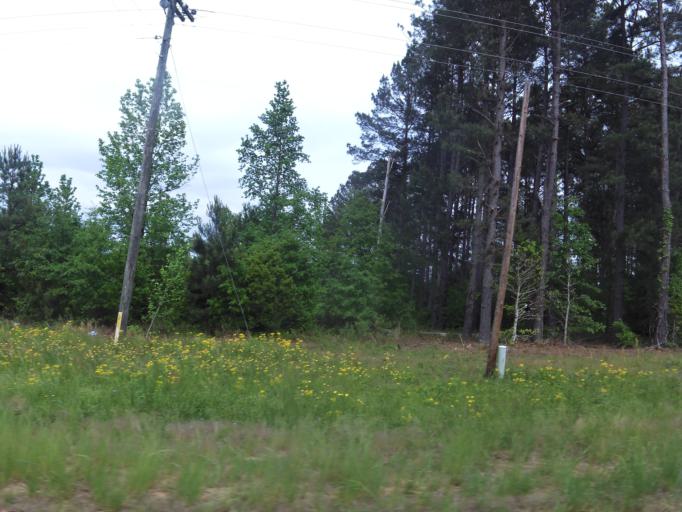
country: US
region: Georgia
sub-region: McDuffie County
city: Thomson
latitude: 33.3463
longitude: -82.4598
